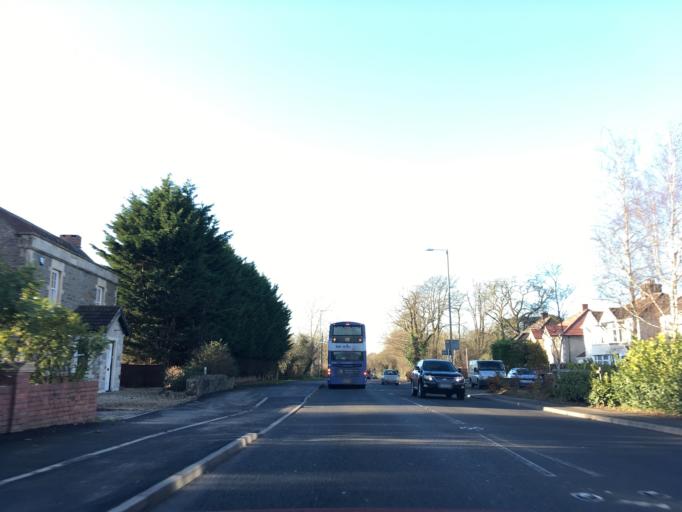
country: GB
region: England
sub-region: Bath and North East Somerset
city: Saltford
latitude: 51.4108
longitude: -2.4770
